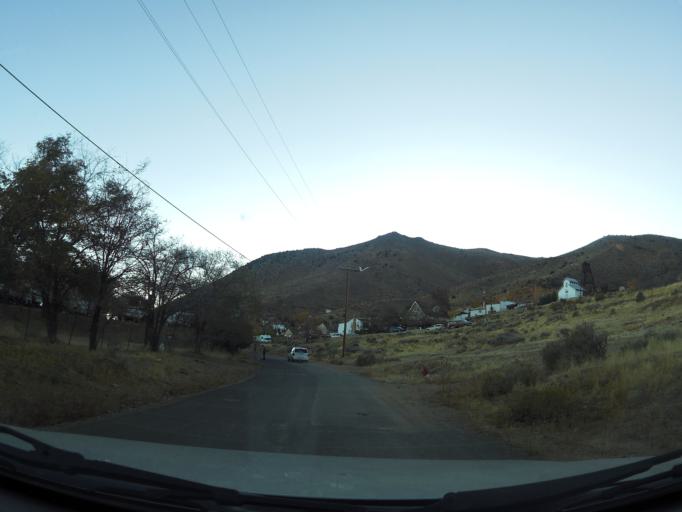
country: US
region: Nevada
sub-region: Storey County
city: Virginia City
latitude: 39.3163
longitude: -119.6455
